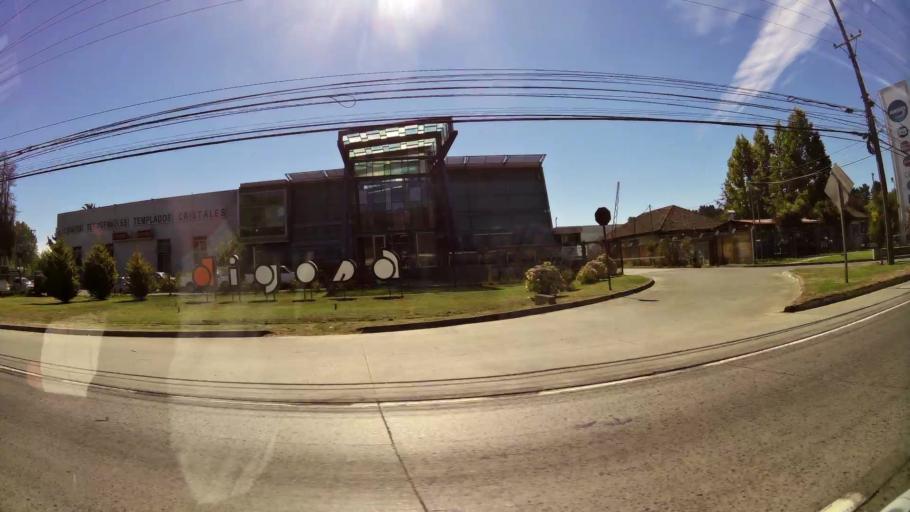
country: CL
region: Biobio
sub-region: Provincia de Concepcion
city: Penco
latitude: -36.7772
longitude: -73.0181
